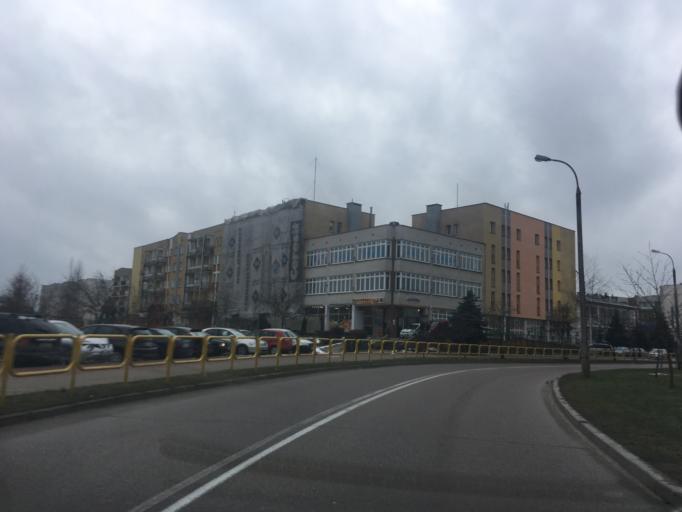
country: PL
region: Podlasie
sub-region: Suwalki
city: Suwalki
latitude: 54.1258
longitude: 22.9358
